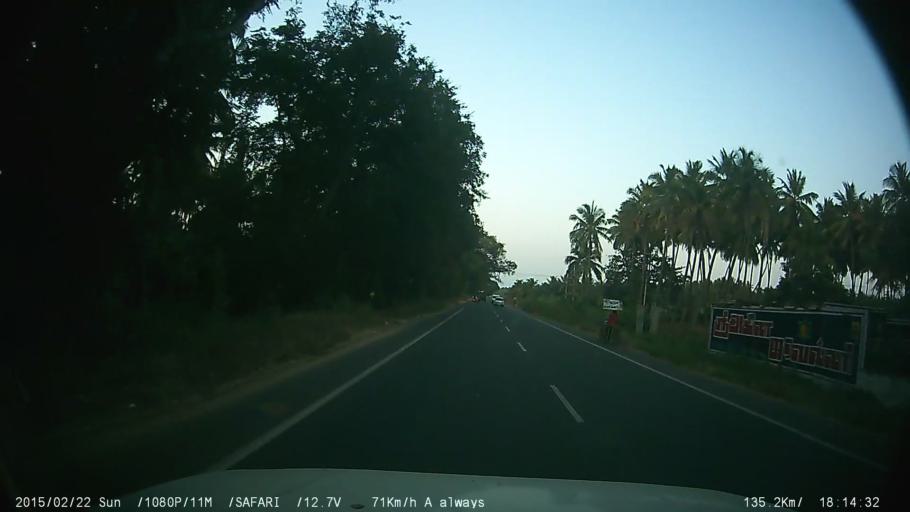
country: IN
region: Tamil Nadu
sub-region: Theni
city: Chinnamanur
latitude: 9.8592
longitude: 77.3885
